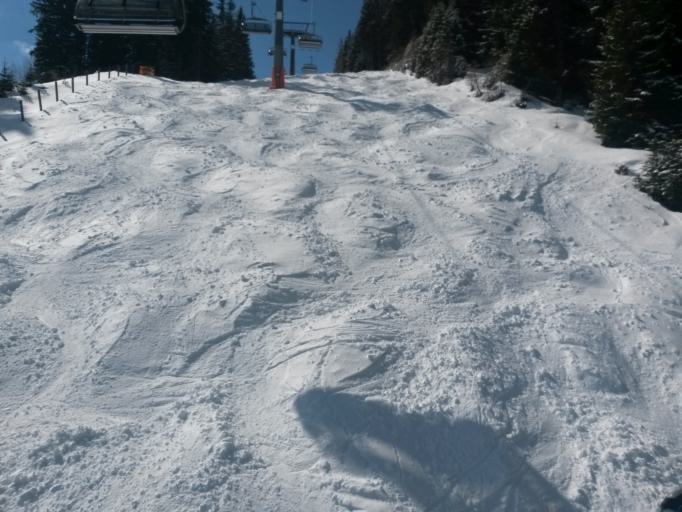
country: AT
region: Salzburg
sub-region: Politischer Bezirk Sankt Johann im Pongau
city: Dorfgastein
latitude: 47.2363
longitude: 13.1751
